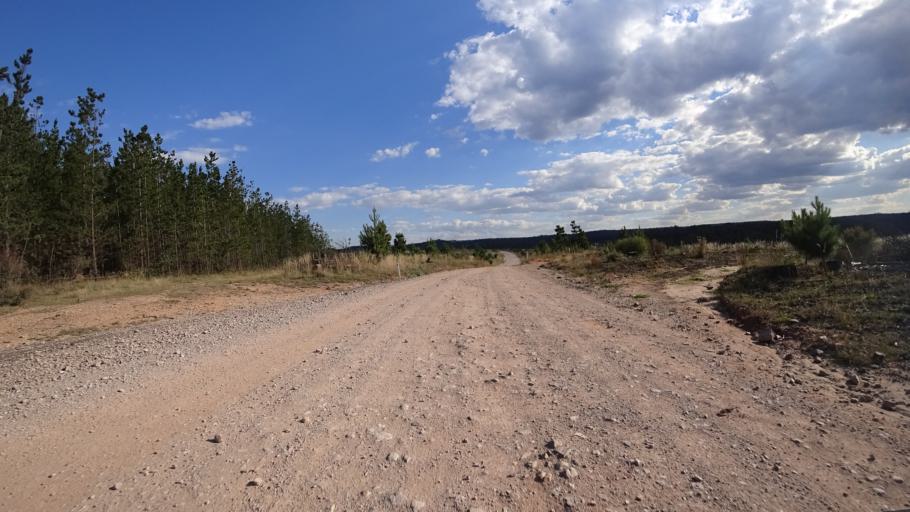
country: AU
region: New South Wales
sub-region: Lithgow
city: Lithgow
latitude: -33.3739
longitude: 150.2450
